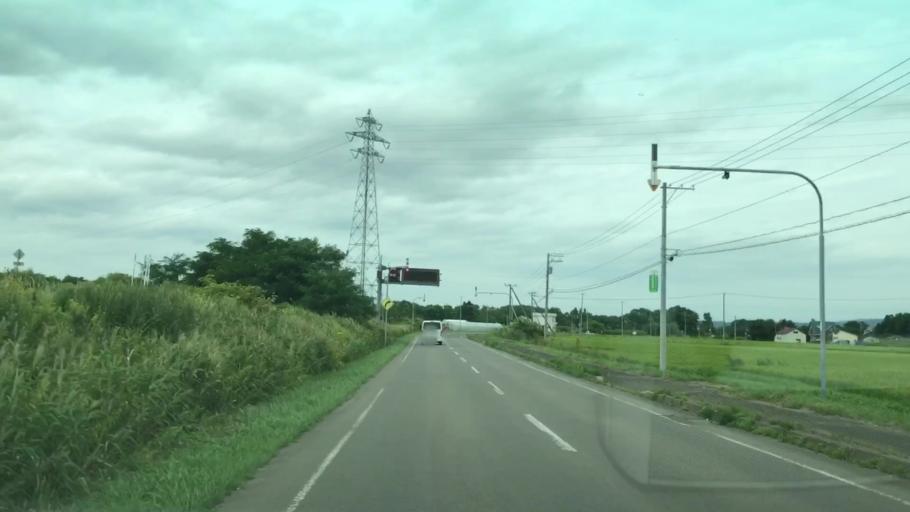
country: JP
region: Hokkaido
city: Iwanai
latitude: 42.9855
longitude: 140.6123
